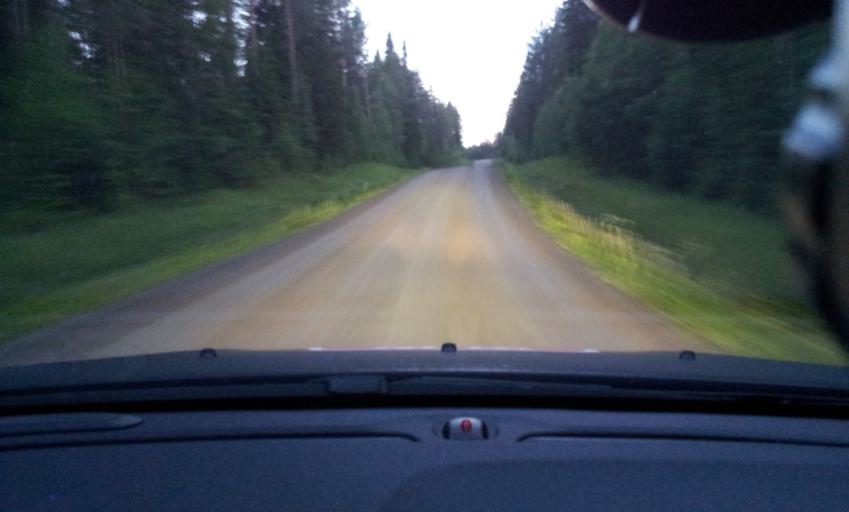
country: SE
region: Vaesternorrland
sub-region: Ange Kommun
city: Ange
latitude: 62.7705
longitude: 15.8949
